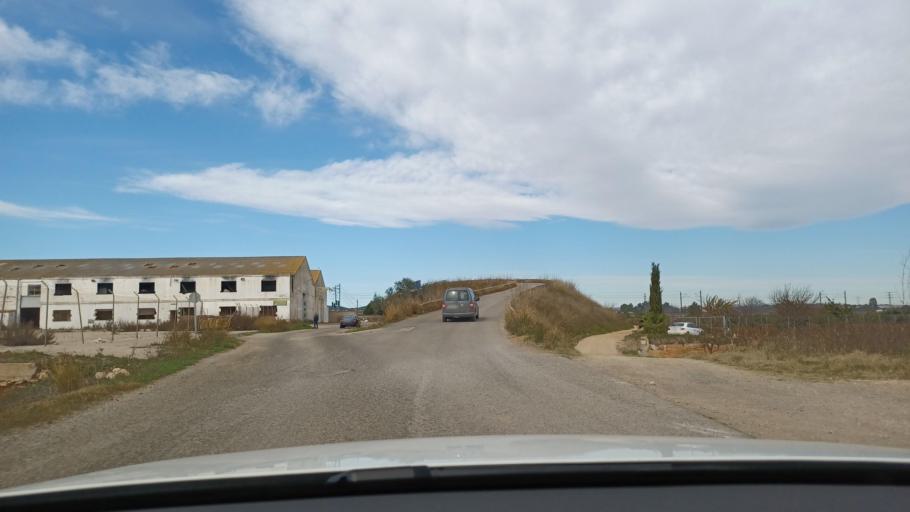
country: ES
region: Valencia
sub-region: Provincia de Valencia
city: Benifaio
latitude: 39.2906
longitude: -0.4353
